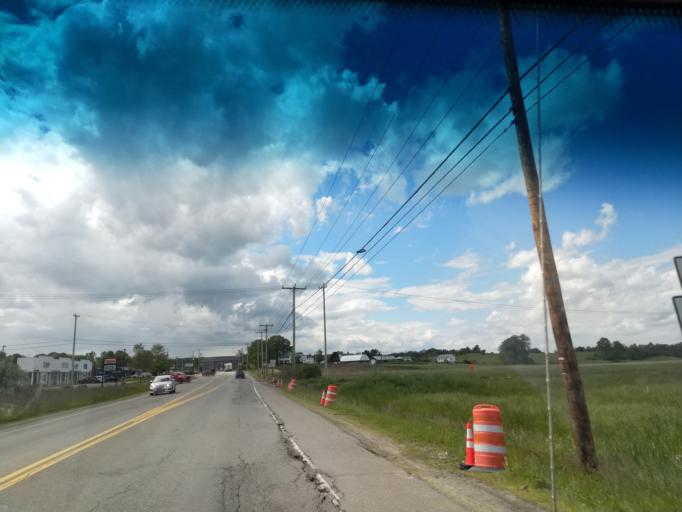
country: US
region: Maine
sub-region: Cumberland County
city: Westbrook
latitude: 43.6895
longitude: -70.3974
